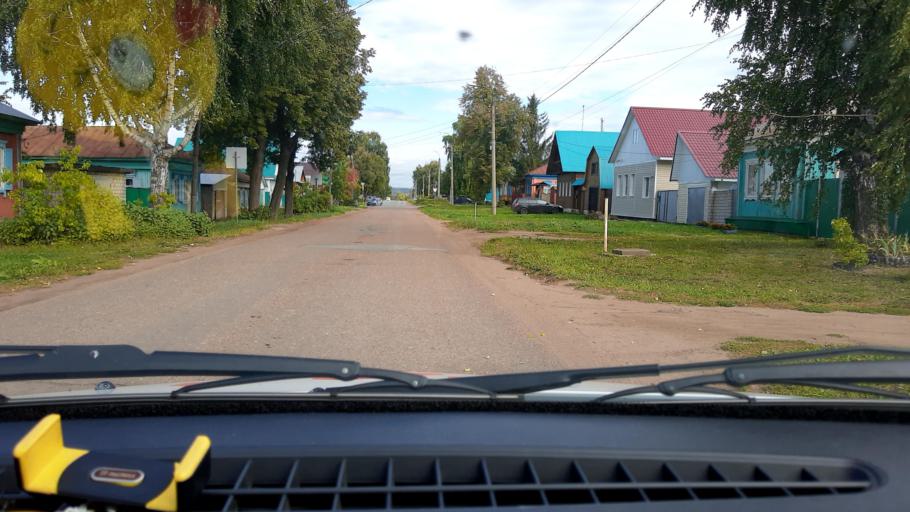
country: RU
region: Bashkortostan
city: Blagoveshchensk
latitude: 55.0310
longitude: 55.9833
